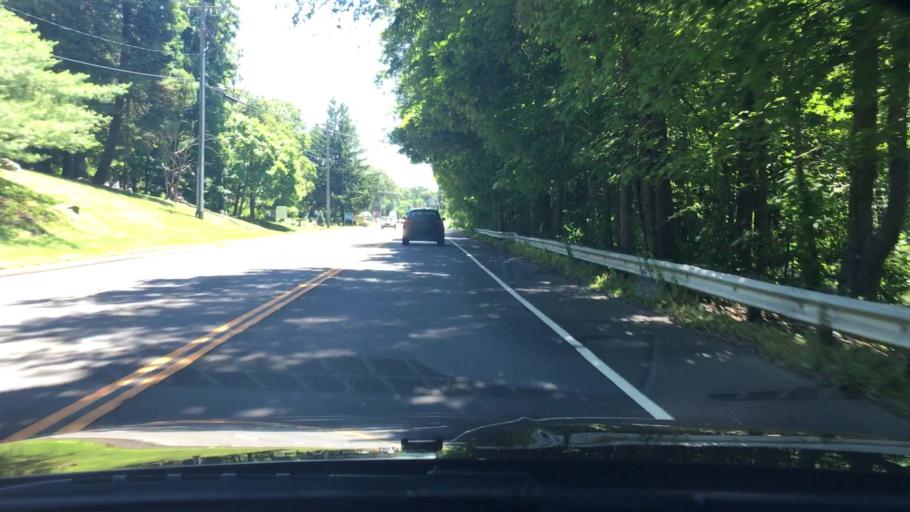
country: US
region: Connecticut
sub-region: Fairfield County
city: Wilton
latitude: 41.1732
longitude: -73.4166
